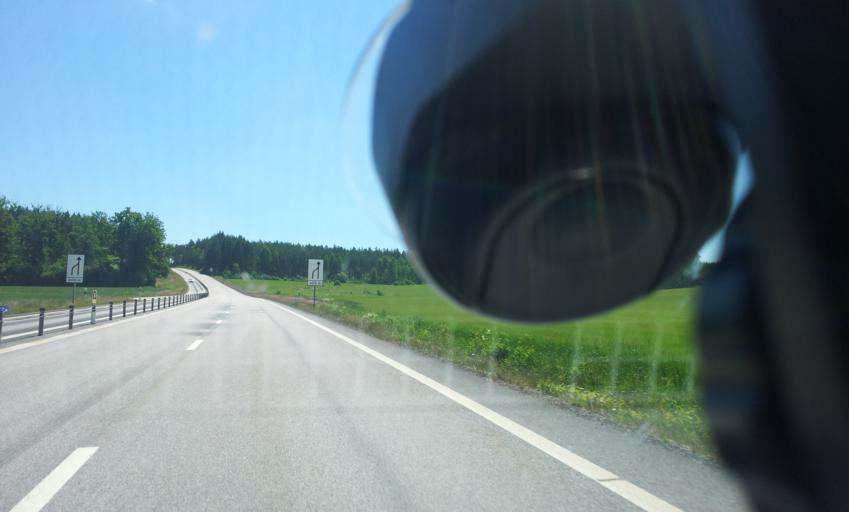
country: SE
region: Kalmar
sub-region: Vasterviks Kommun
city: Forserum
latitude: 58.0707
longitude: 16.5200
